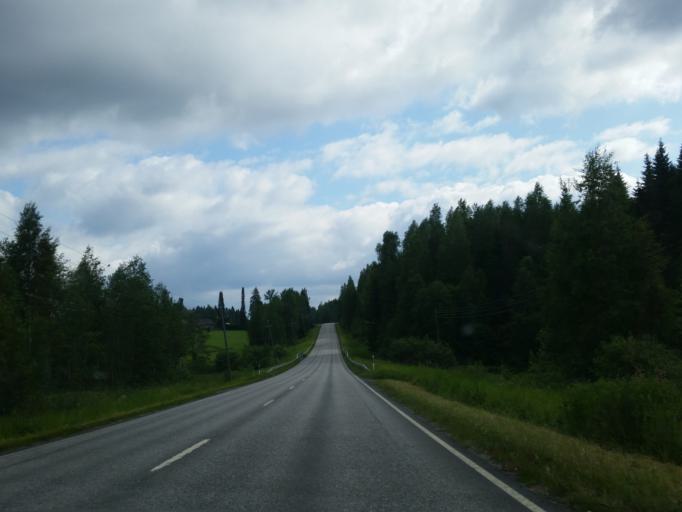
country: FI
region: Northern Savo
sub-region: Kuopio
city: Kuopio
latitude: 62.8460
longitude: 27.5243
